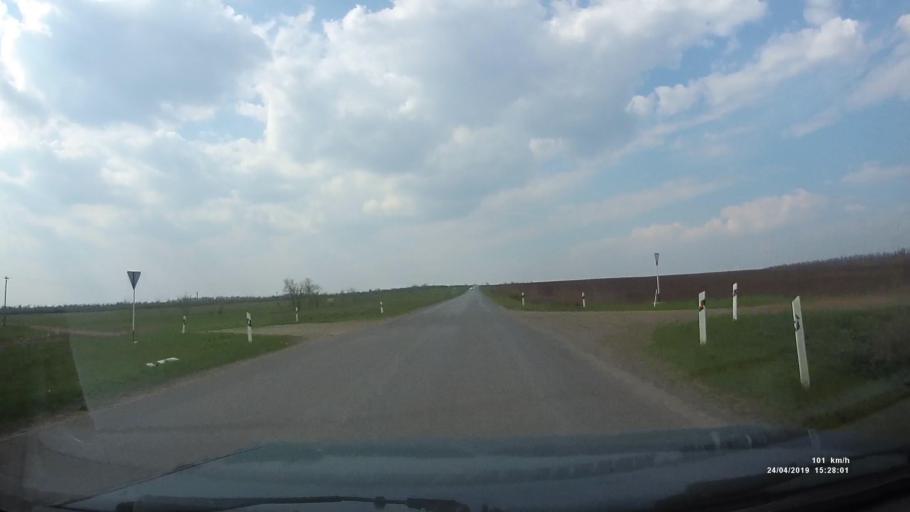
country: RU
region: Rostov
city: Remontnoye
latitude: 46.5731
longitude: 43.0214
